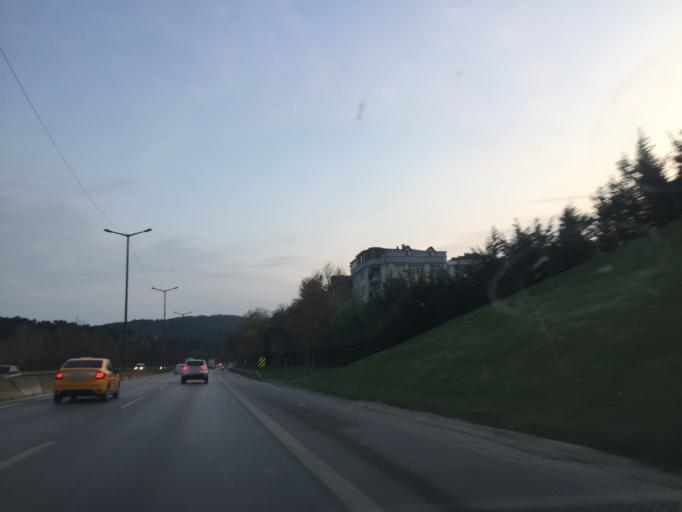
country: TR
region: Istanbul
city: Samandira
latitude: 40.9599
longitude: 29.2212
